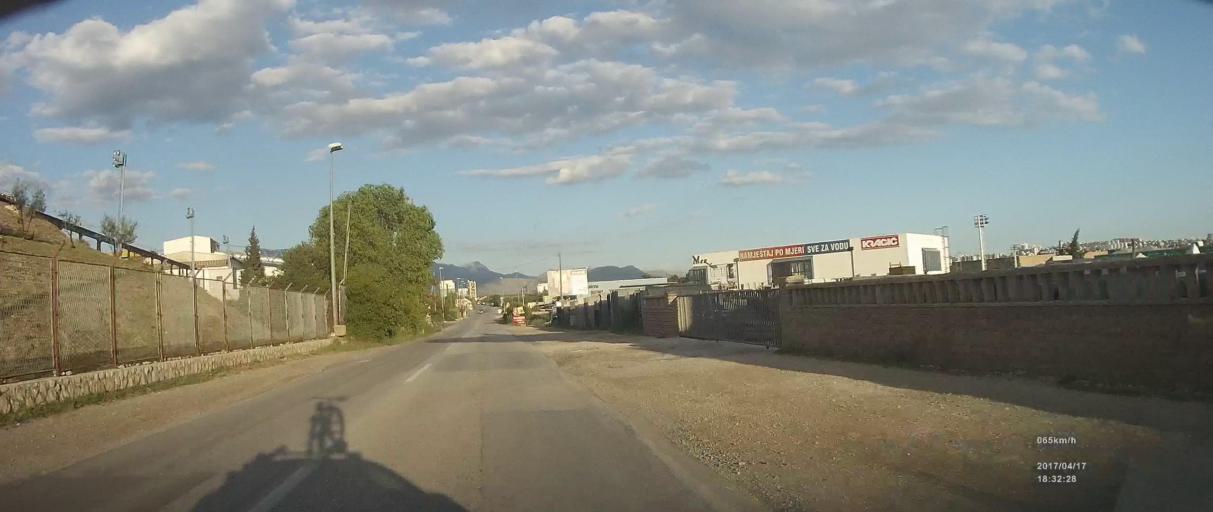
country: HR
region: Splitsko-Dalmatinska
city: Vranjic
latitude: 43.5423
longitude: 16.4464
